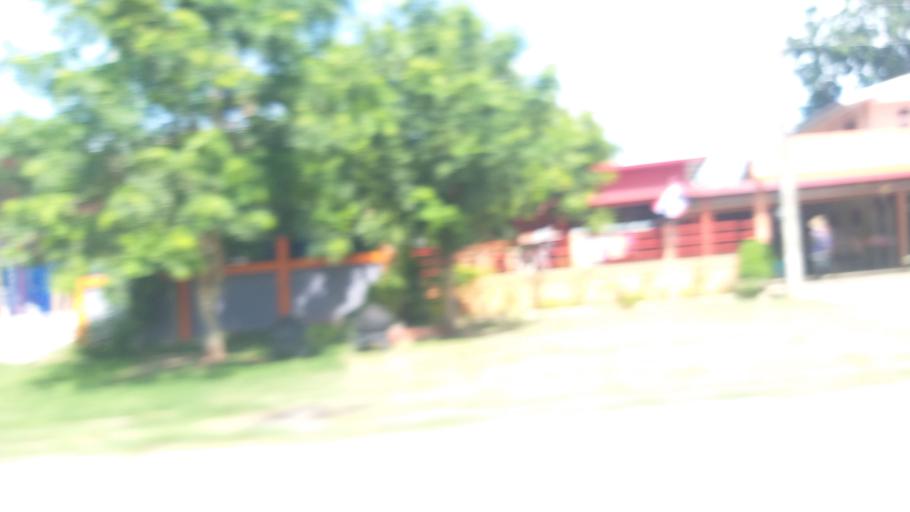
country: TH
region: Khon Kaen
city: Nong Ruea
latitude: 16.4683
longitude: 102.4417
